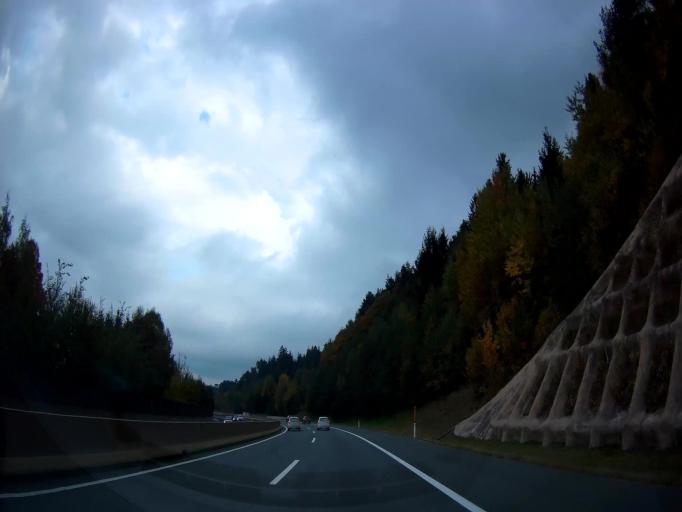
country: AT
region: Styria
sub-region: Politischer Bezirk Voitsberg
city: Ligist
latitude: 46.9718
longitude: 15.1987
